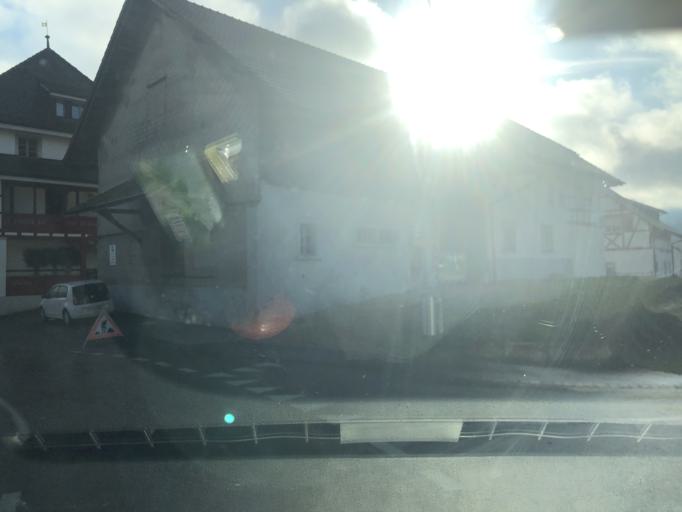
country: CH
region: Aargau
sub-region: Bezirk Baden
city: Unterehrendingen
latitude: 47.5200
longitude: 8.3615
